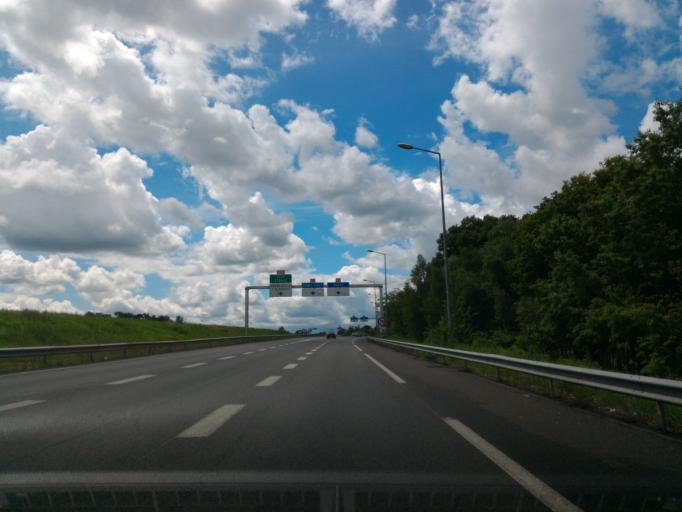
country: FR
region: Ile-de-France
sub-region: Departement de Seine-et-Marne
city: Lognes
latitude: 48.8335
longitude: 2.6214
